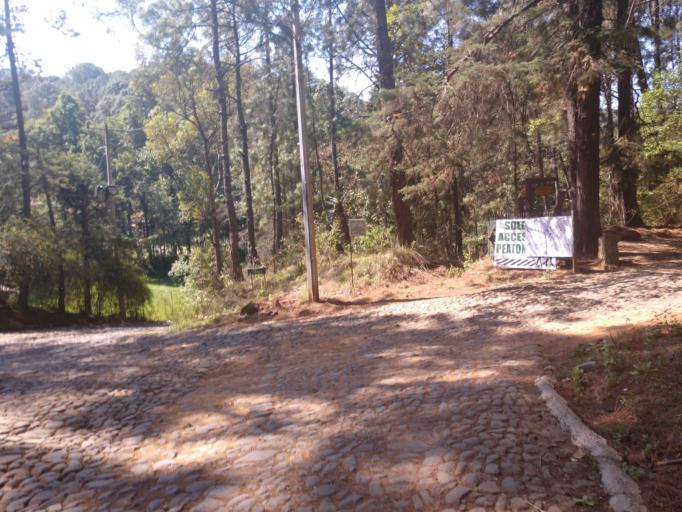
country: MX
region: Jalisco
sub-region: Mazamitla
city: Mazamitla
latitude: 19.9021
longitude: -103.0321
